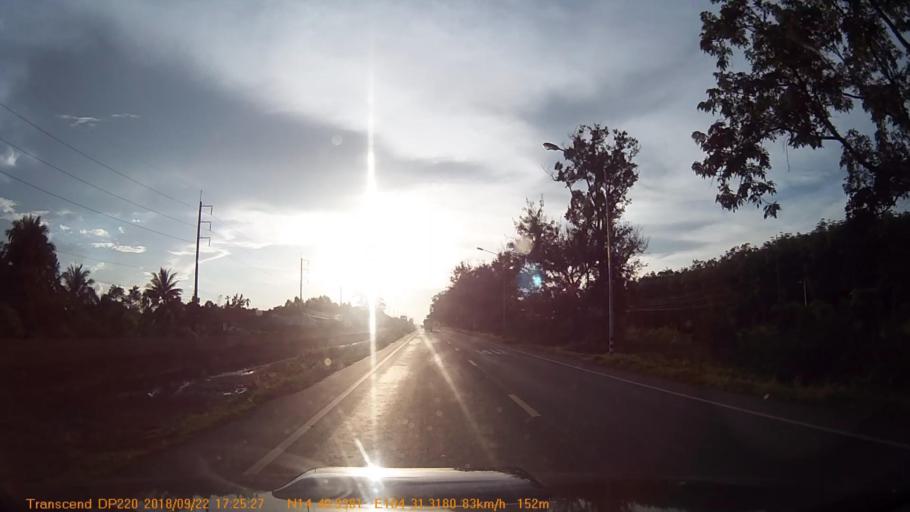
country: TH
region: Sisaket
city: Khun Han
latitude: 14.6823
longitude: 104.5216
